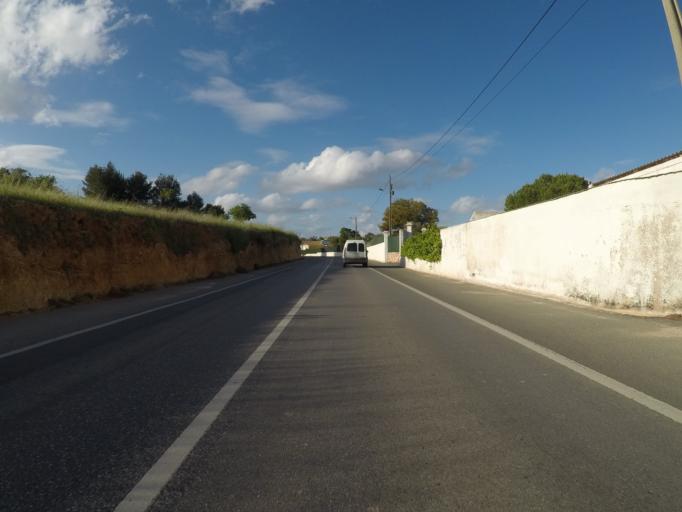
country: PT
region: Faro
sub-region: Lagoa
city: Carvoeiro
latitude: 37.1125
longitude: -8.4553
